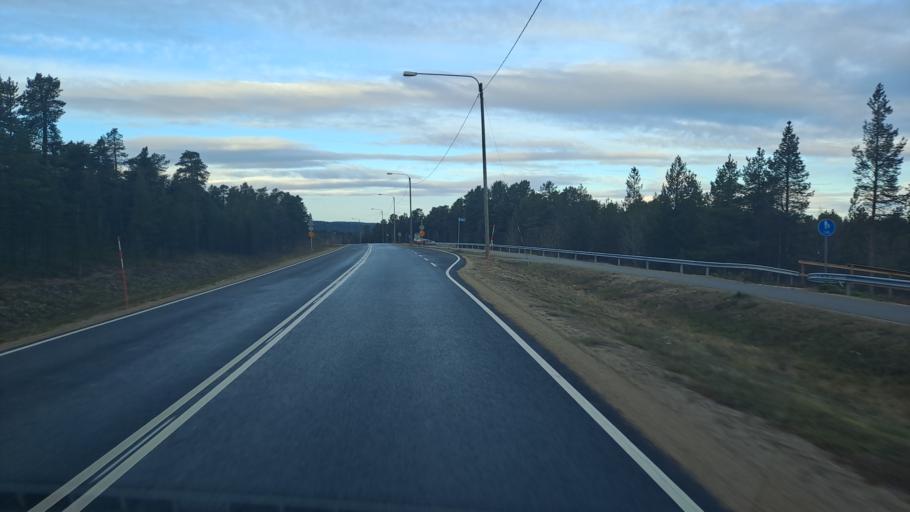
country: FI
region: Lapland
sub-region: Pohjois-Lappi
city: Inari
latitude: 68.9007
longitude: 27.0748
